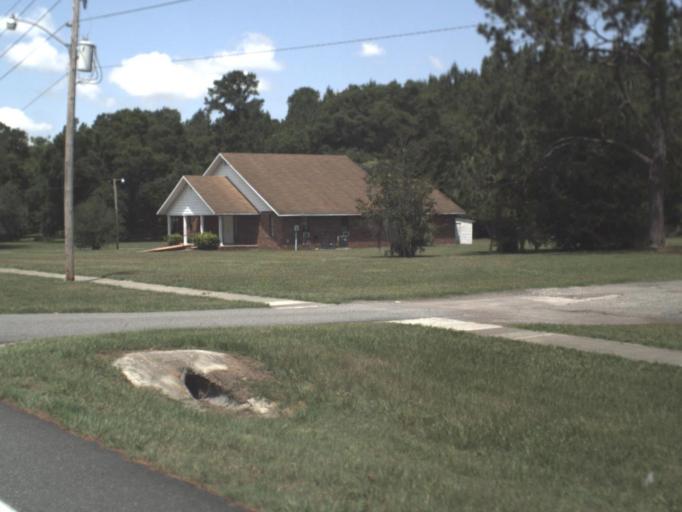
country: US
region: Florida
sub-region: Levy County
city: Williston
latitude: 29.3975
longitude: -82.4436
